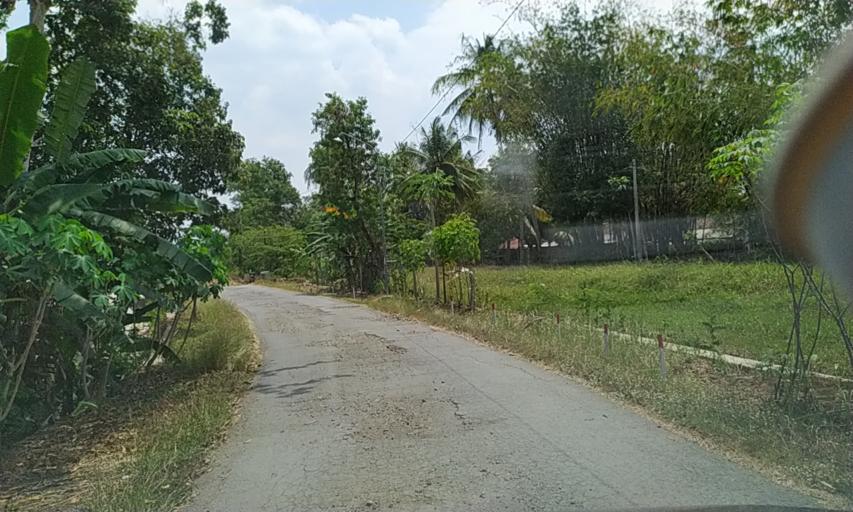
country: ID
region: Central Java
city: Kedungreja
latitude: -7.5012
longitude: 108.7772
